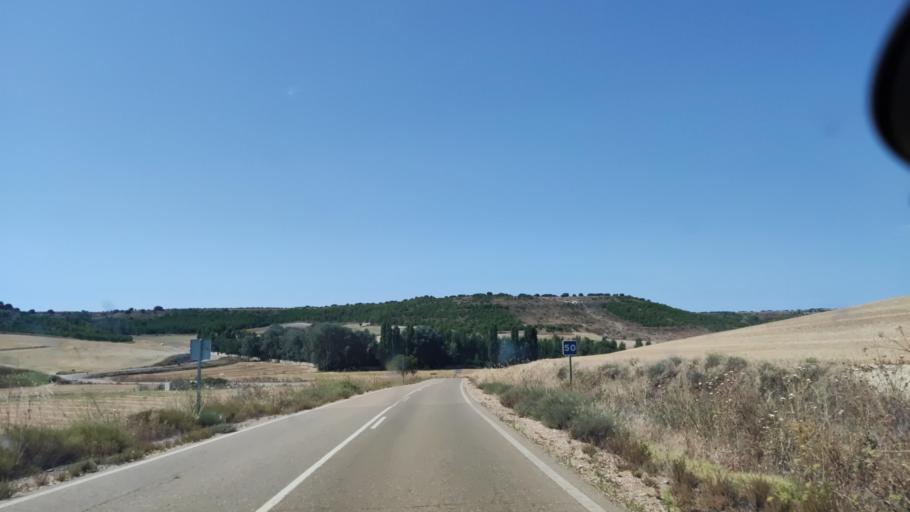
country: ES
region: Castille and Leon
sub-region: Provincia de Valladolid
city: Uruena
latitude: 41.7224
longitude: -5.1937
